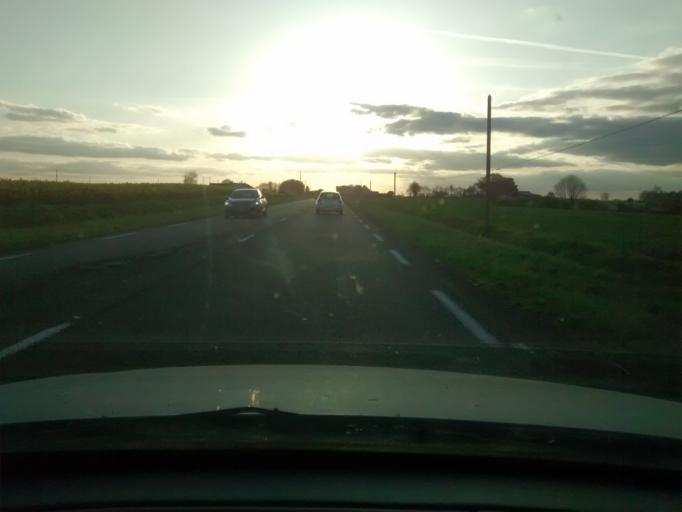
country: FR
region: Pays de la Loire
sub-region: Departement de la Mayenne
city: Sainte-Suzanne
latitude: 48.0328
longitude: -0.3441
